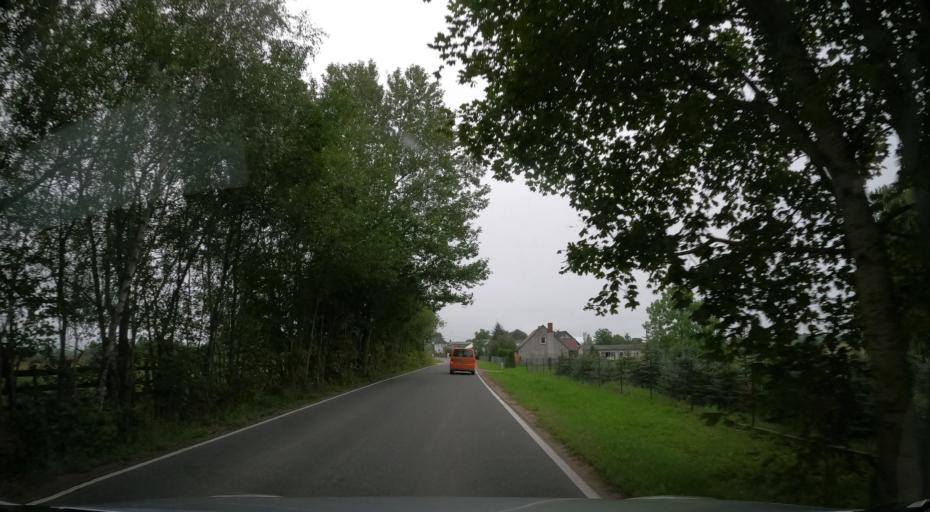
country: PL
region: Pomeranian Voivodeship
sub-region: Powiat wejherowski
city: Szemud
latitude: 54.5016
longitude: 18.1711
